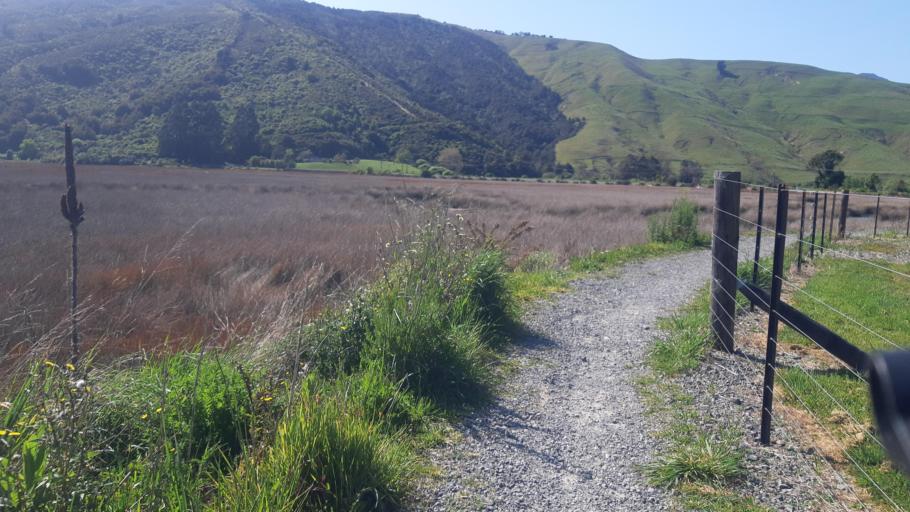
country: NZ
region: Marlborough
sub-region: Marlborough District
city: Picton
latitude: -41.2852
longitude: 173.7706
